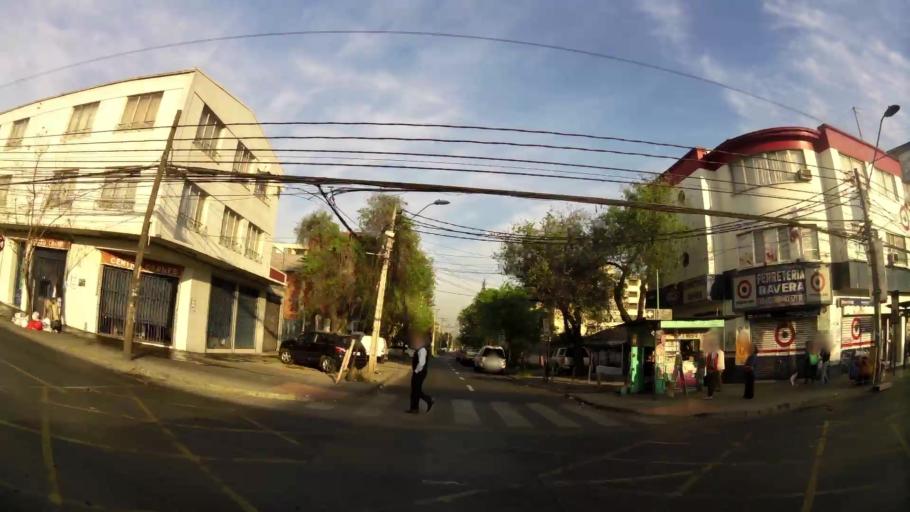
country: CL
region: Santiago Metropolitan
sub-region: Provincia de Santiago
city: Santiago
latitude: -33.5016
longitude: -70.6545
